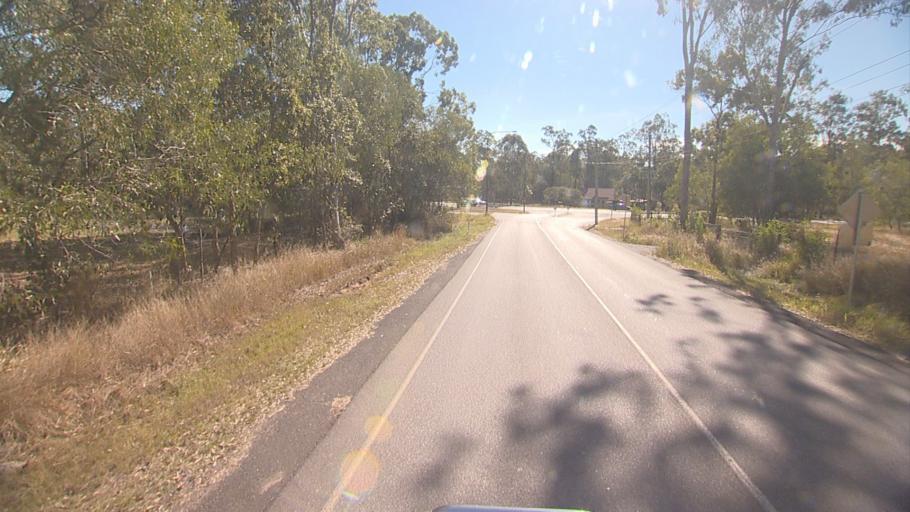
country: AU
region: Queensland
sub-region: Logan
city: North Maclean
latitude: -27.8180
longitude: 152.9707
